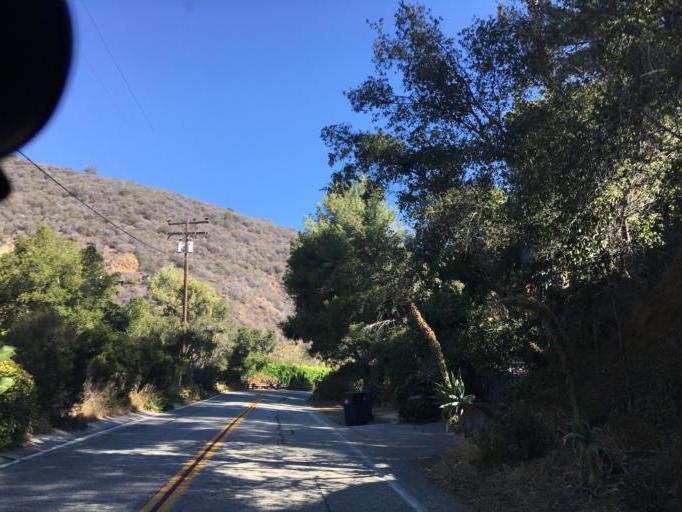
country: US
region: California
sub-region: Ventura County
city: Casa Conejo
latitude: 34.0803
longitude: -118.9211
